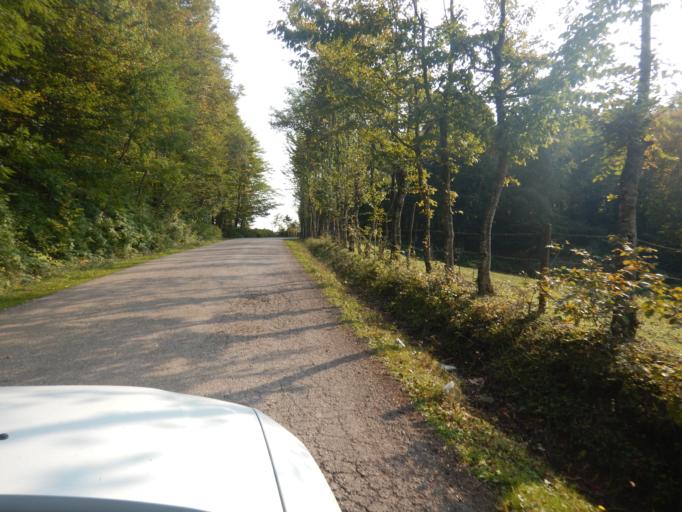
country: TR
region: Ordu
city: Golkoy
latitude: 40.6599
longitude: 37.5580
